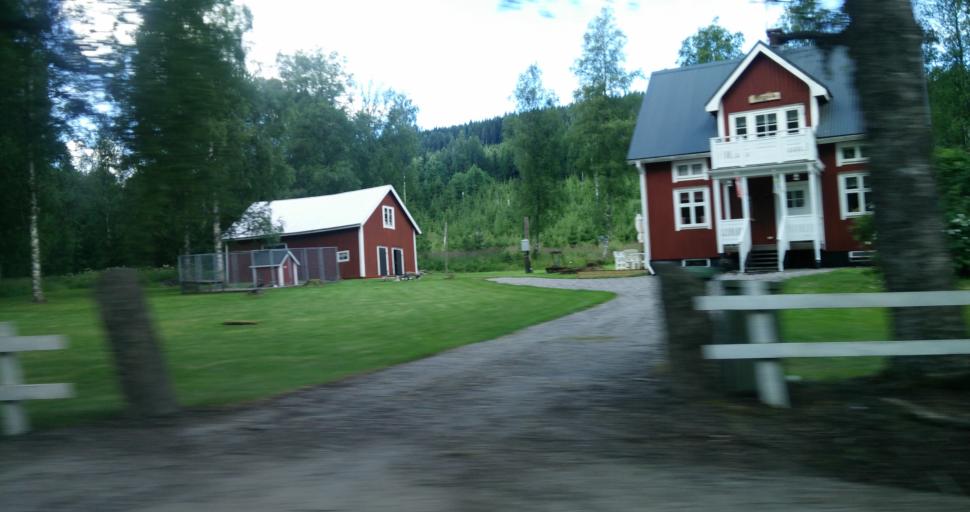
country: SE
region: Vaermland
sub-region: Hagfors Kommun
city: Ekshaerad
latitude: 60.0687
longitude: 13.4759
